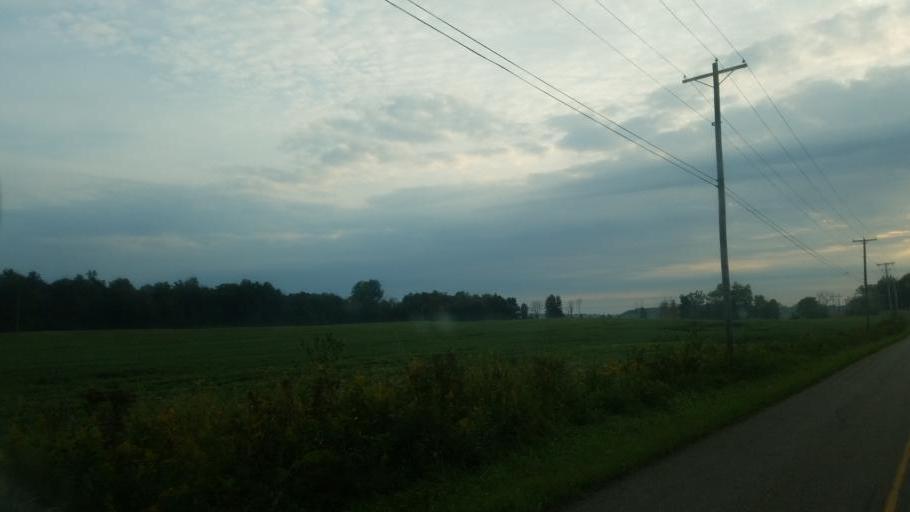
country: US
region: Ohio
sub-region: Knox County
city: Centerburg
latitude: 40.4037
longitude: -82.6421
